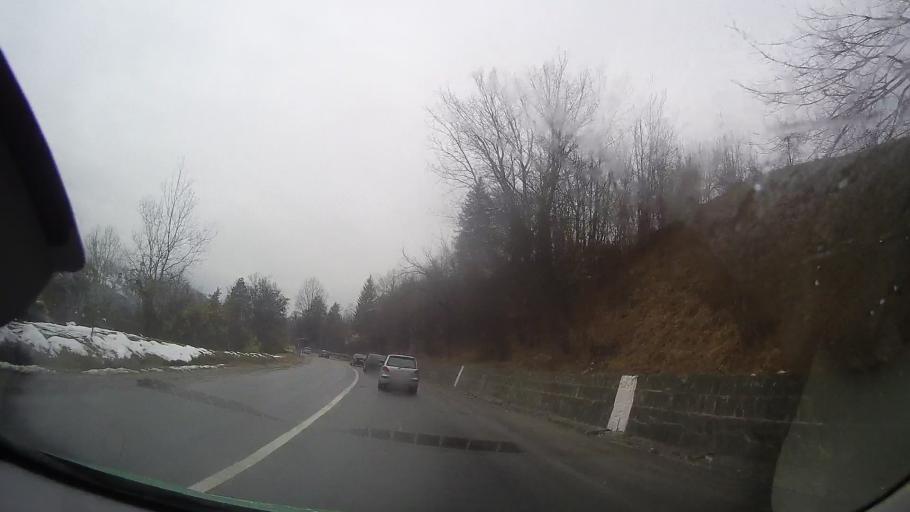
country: RO
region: Neamt
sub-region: Comuna Bicaz
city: Dodeni
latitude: 46.9014
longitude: 26.1176
